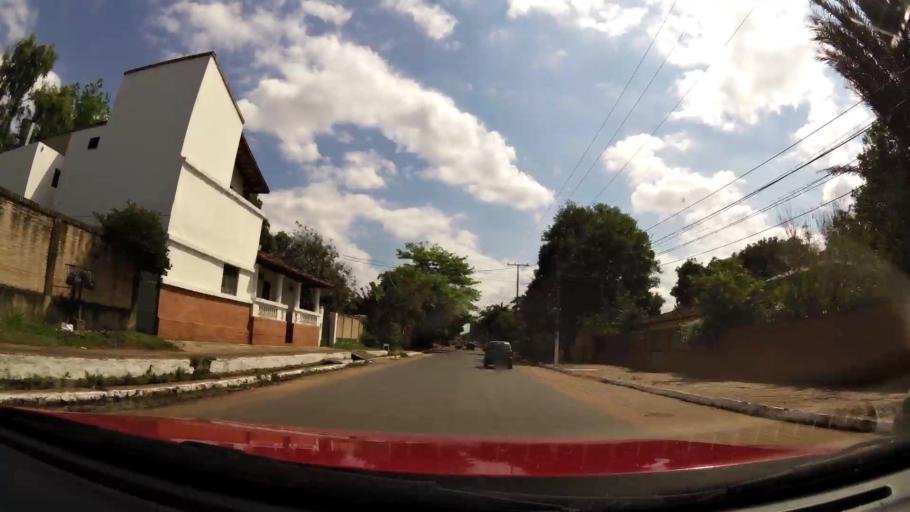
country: PY
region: Central
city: San Lorenzo
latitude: -25.3390
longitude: -57.5098
